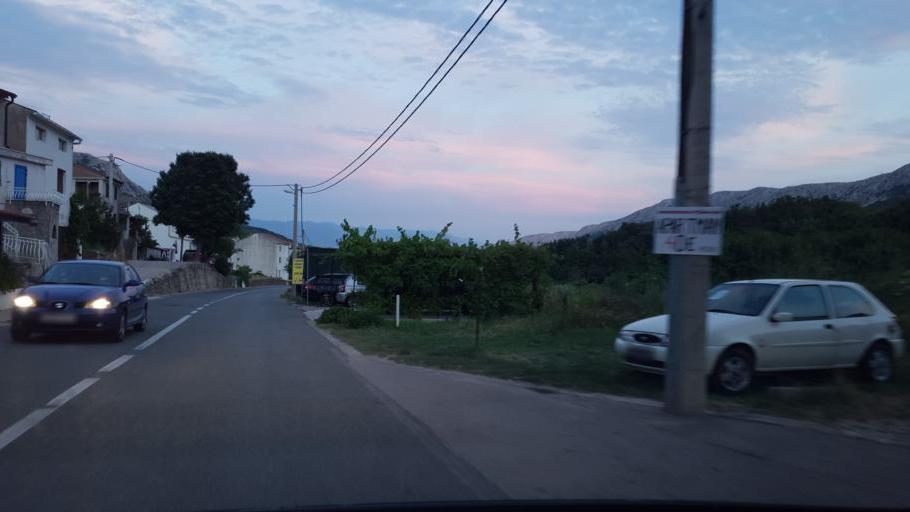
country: HR
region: Primorsko-Goranska
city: Punat
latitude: 44.9947
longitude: 14.7164
